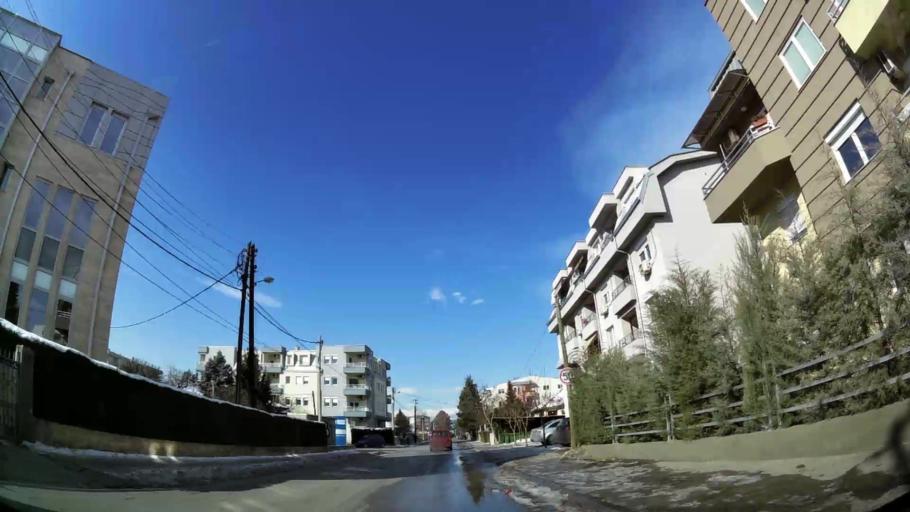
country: MK
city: Krushopek
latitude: 42.0043
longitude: 21.3691
